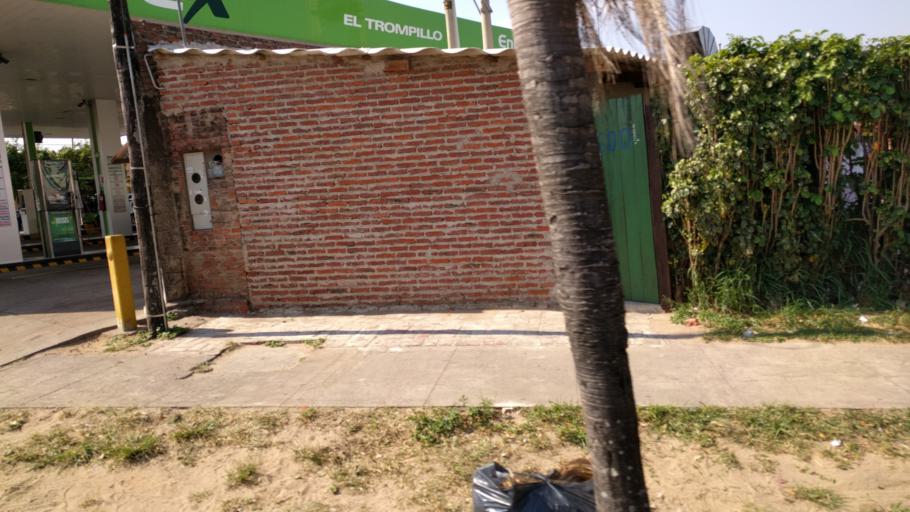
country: BO
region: Santa Cruz
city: Santa Cruz de la Sierra
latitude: -17.8076
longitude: -63.1708
